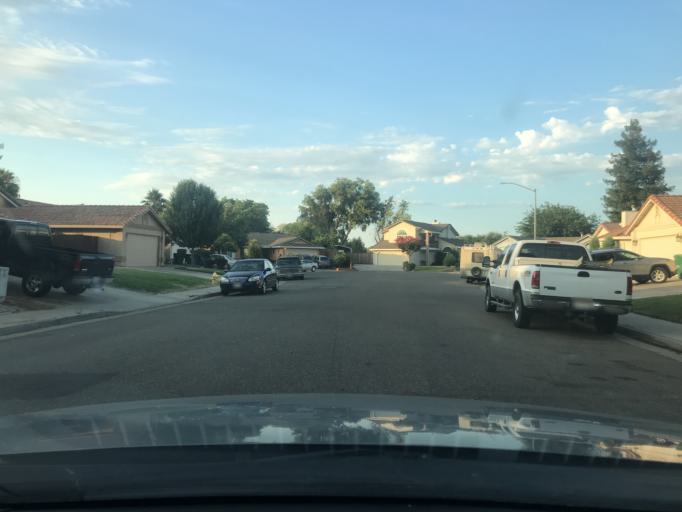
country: US
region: California
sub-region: Merced County
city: Merced
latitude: 37.3290
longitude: -120.5390
